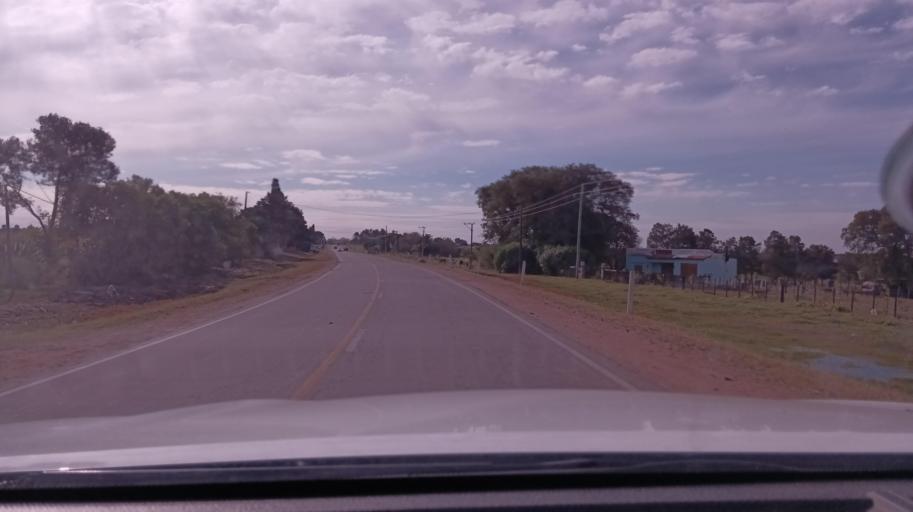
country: UY
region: Canelones
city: Toledo
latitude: -34.7279
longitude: -56.1131
